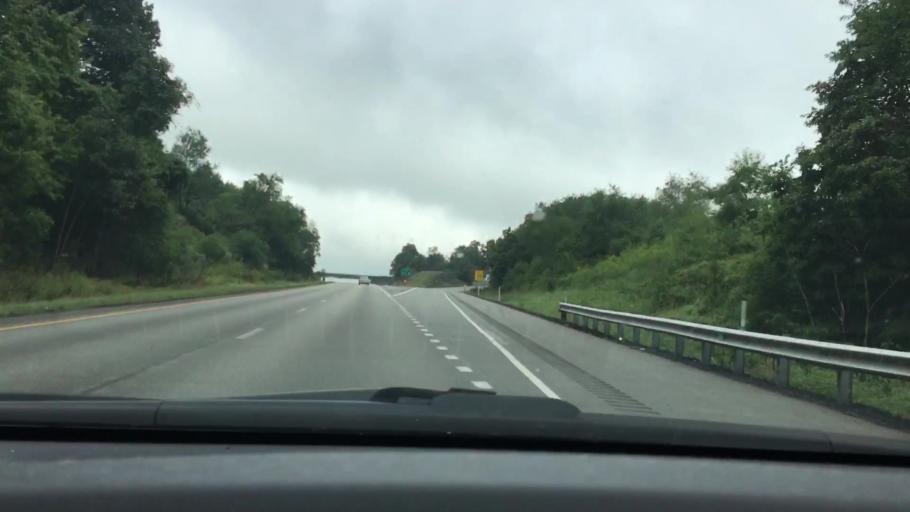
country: US
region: Pennsylvania
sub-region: Butler County
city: Zelienople
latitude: 40.7559
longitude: -80.1116
